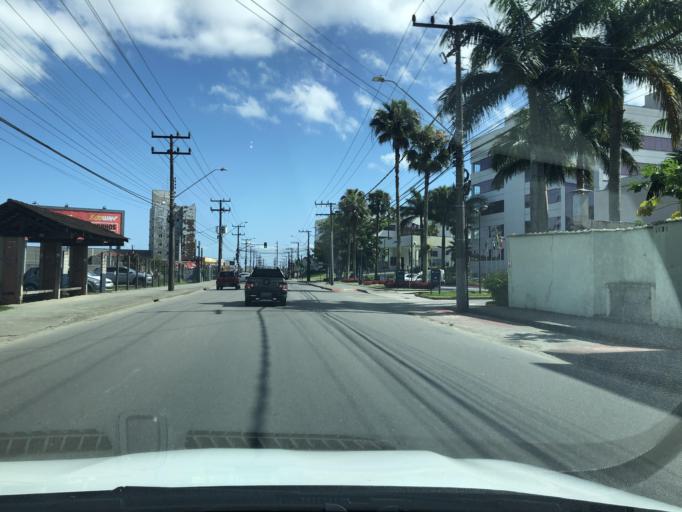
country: BR
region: Santa Catarina
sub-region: Joinville
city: Joinville
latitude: -26.2631
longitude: -48.8513
